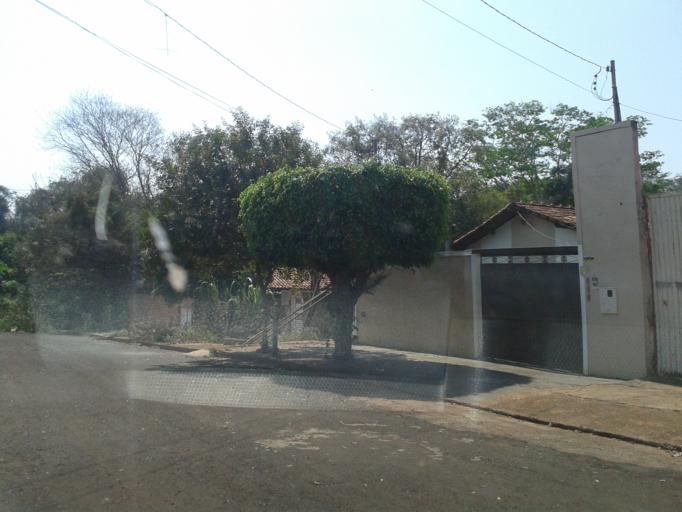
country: BR
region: Minas Gerais
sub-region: Ituiutaba
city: Ituiutaba
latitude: -18.9675
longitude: -49.4835
